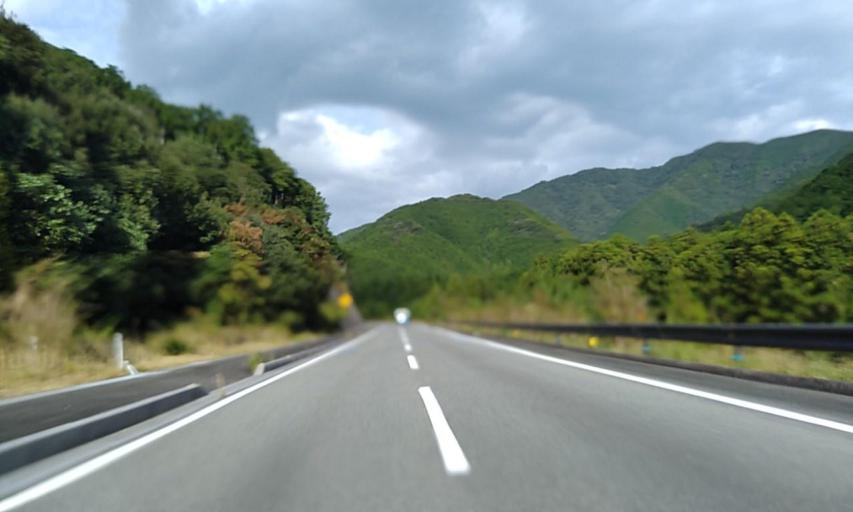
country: JP
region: Mie
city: Owase
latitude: 34.2350
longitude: 136.3987
